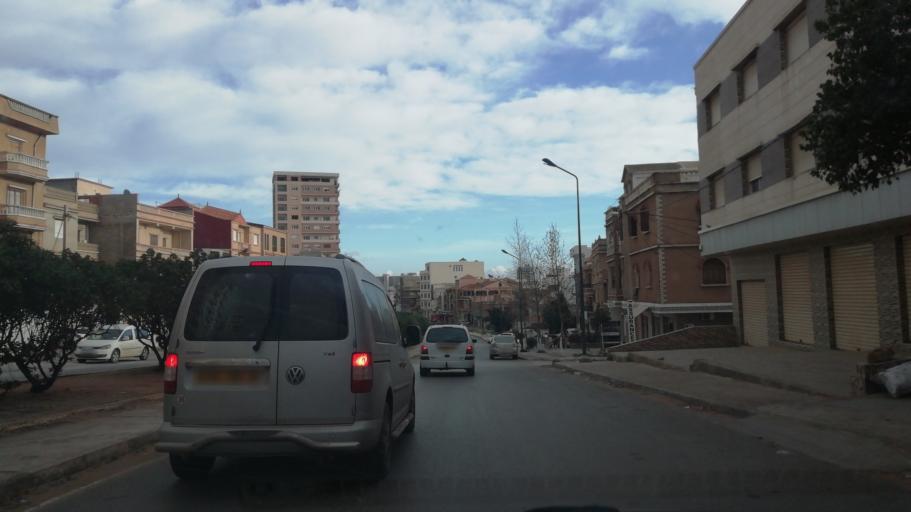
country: DZ
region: Oran
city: Bir el Djir
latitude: 35.7197
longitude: -0.5826
